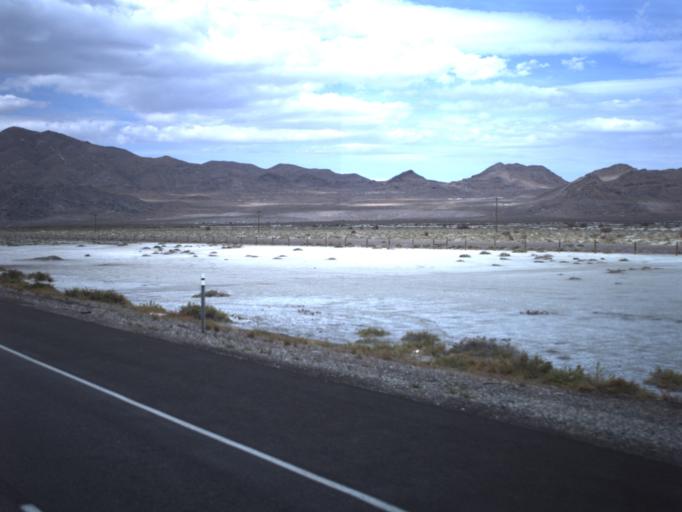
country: US
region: Utah
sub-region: Tooele County
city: Wendover
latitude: 40.7441
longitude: -113.9841
